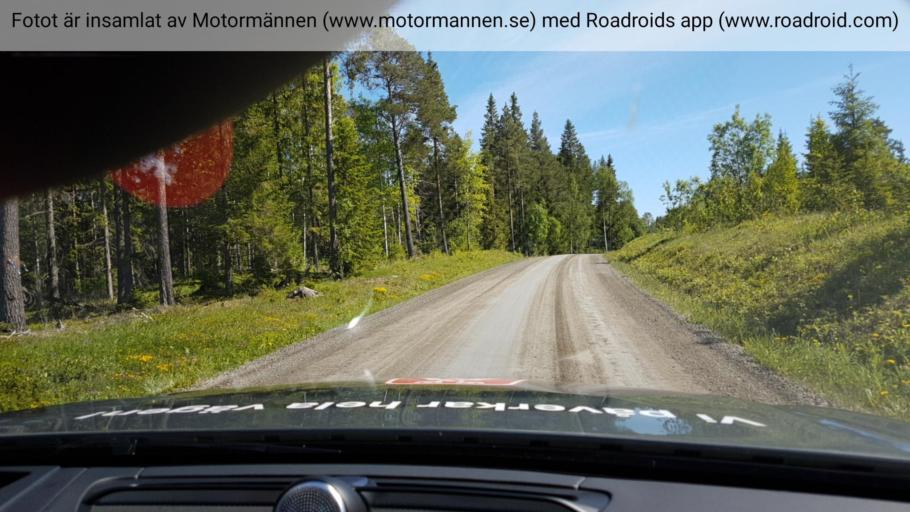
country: SE
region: Jaemtland
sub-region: OEstersunds Kommun
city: Brunflo
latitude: 63.0067
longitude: 14.7917
